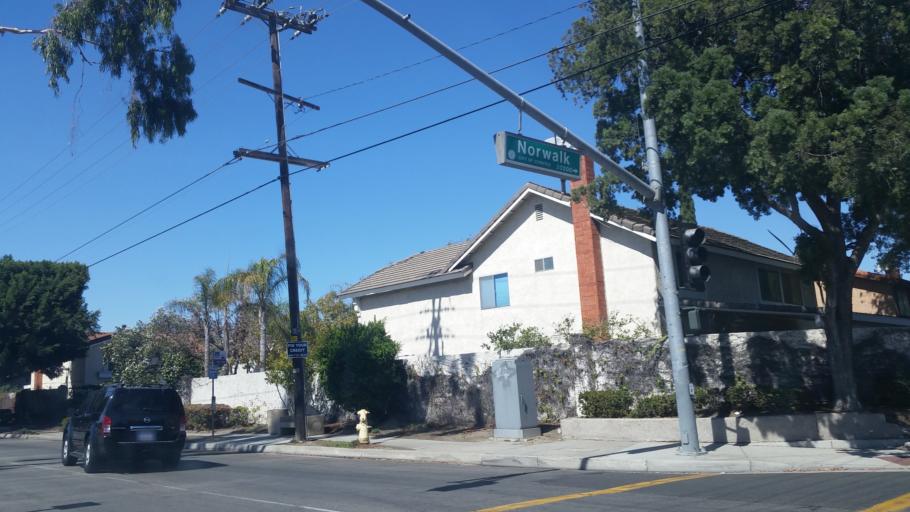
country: US
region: California
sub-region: Los Angeles County
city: Cerritos
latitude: 33.8462
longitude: -118.0722
